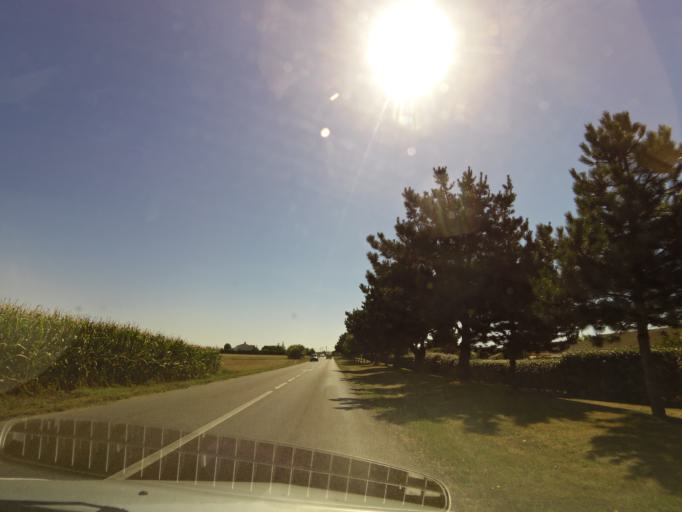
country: FR
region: Pays de la Loire
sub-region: Departement de la Vendee
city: Jard-sur-Mer
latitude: 46.4192
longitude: -1.5569
